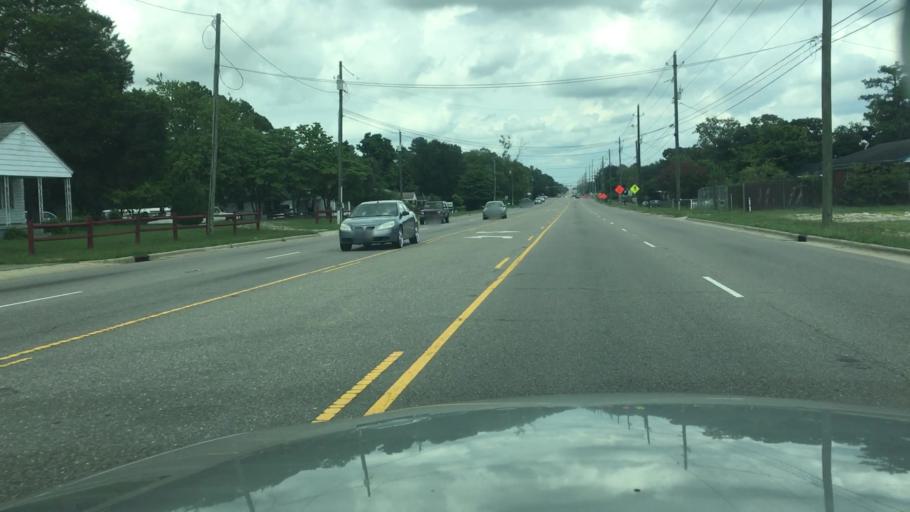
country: US
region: North Carolina
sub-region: Cumberland County
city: Hope Mills
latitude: 35.0119
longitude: -78.9450
